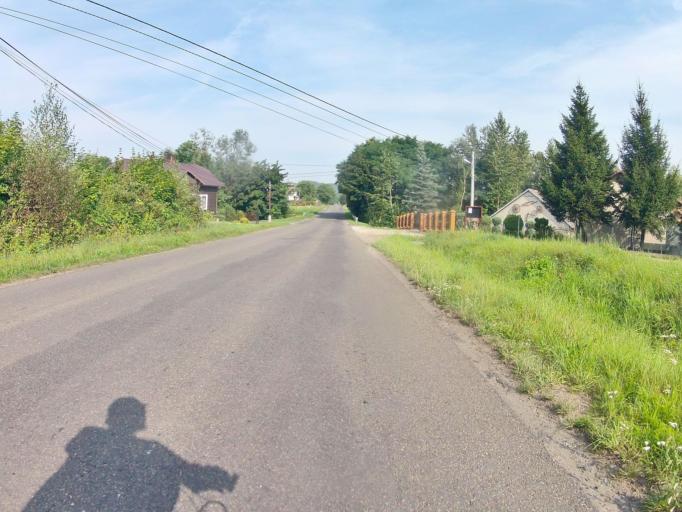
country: PL
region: Subcarpathian Voivodeship
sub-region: Powiat jasielski
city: Kolaczyce
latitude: 49.7858
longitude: 21.4030
